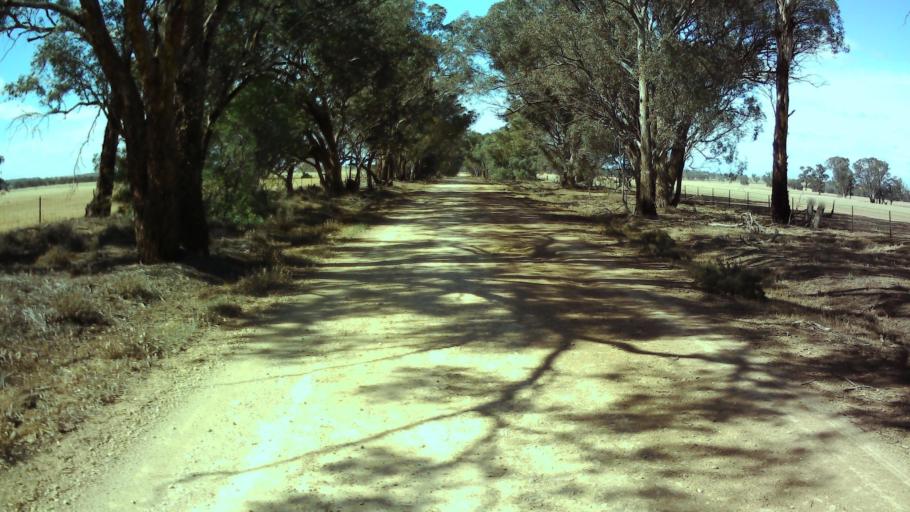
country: AU
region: New South Wales
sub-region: Weddin
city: Grenfell
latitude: -34.0492
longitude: 148.3142
